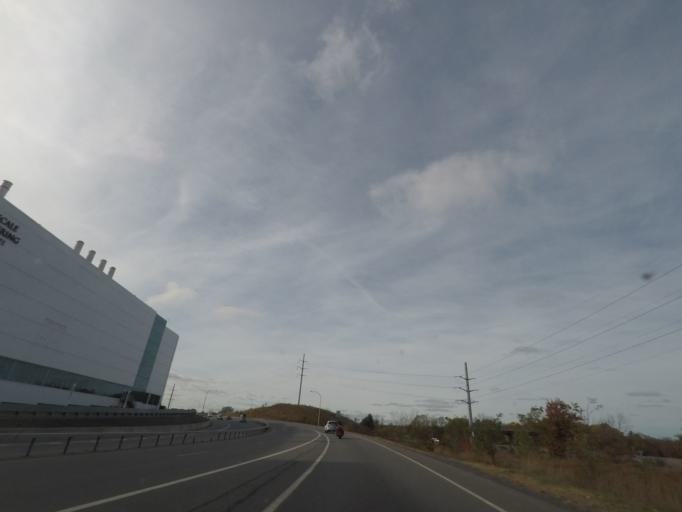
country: US
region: New York
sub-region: Albany County
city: McKownville
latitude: 42.6938
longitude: -73.8328
